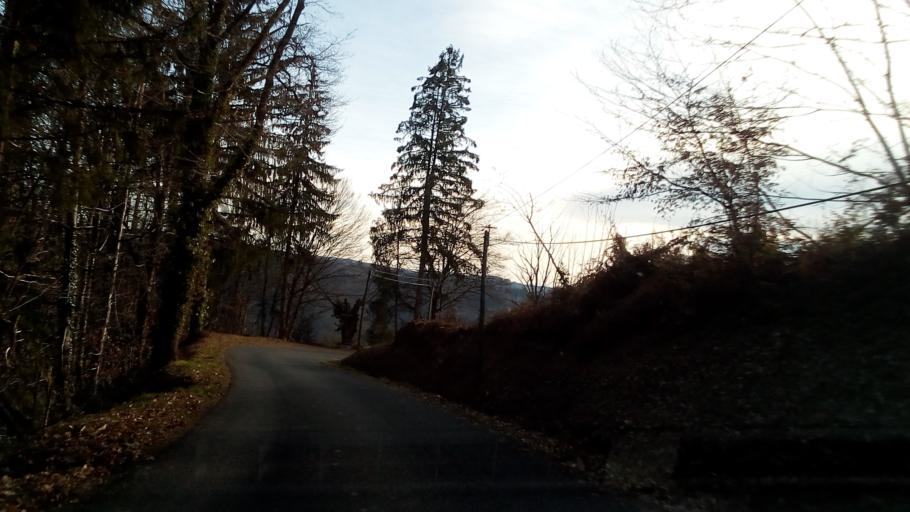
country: FR
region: Limousin
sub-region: Departement de la Correze
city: Naves
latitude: 45.3039
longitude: 1.7829
